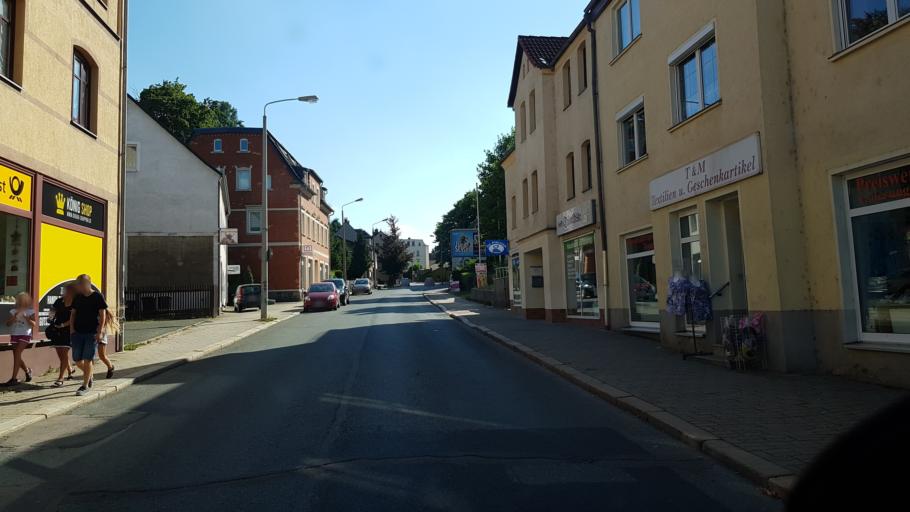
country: DE
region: Saxony
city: Wilkau-Hasslau
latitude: 50.6807
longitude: 12.4745
